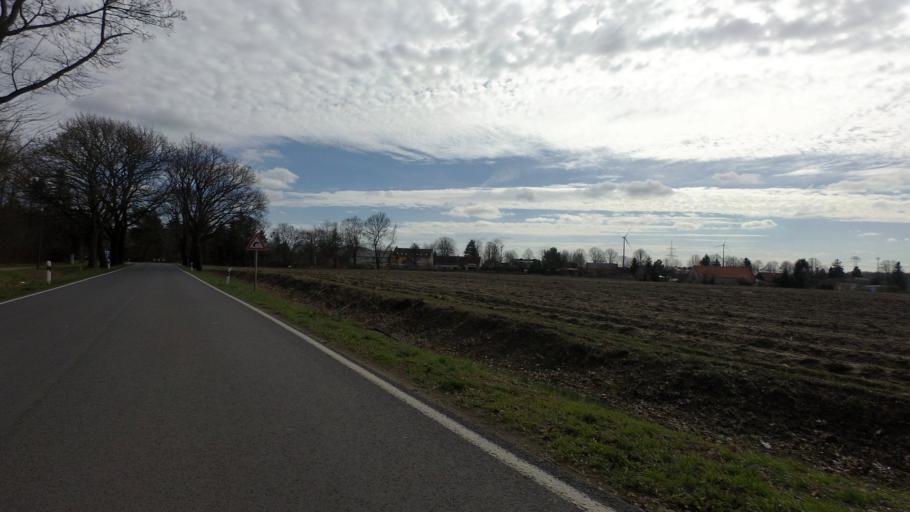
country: DE
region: Berlin
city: Buchholz
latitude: 52.6553
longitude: 13.4327
